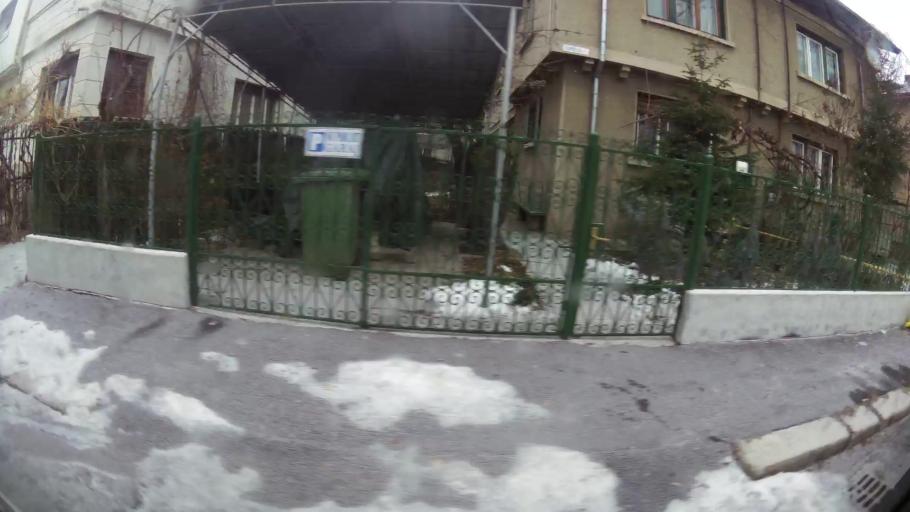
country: RO
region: Prahova
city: Ploiesti
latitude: 44.9433
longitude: 26.0363
